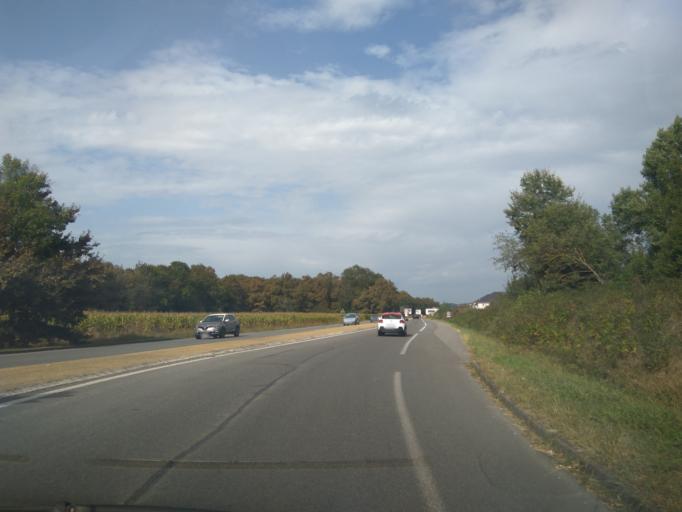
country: FR
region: Aquitaine
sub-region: Departement des Pyrenees-Atlantiques
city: Artiguelouve
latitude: 43.3157
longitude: -0.4577
